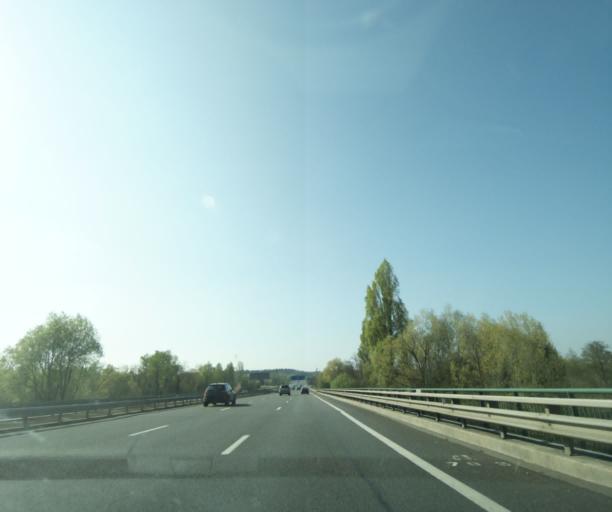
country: FR
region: Ile-de-France
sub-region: Departement de Seine-et-Marne
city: Nemours
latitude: 48.2868
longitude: 2.6917
